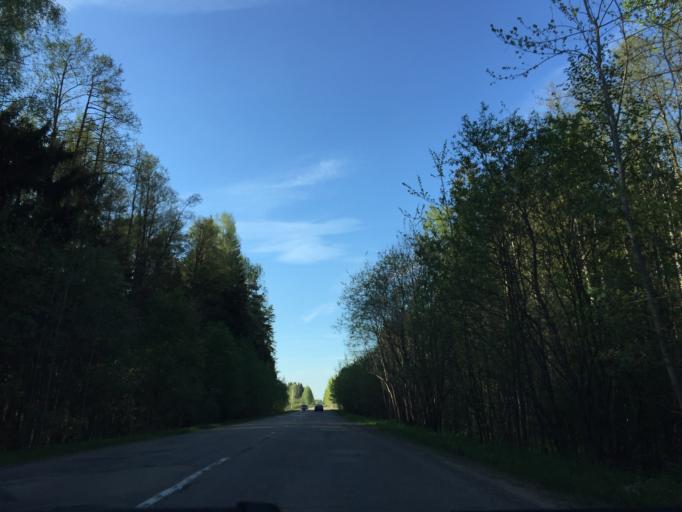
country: LV
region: Lecava
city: Iecava
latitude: 56.7130
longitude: 24.1124
